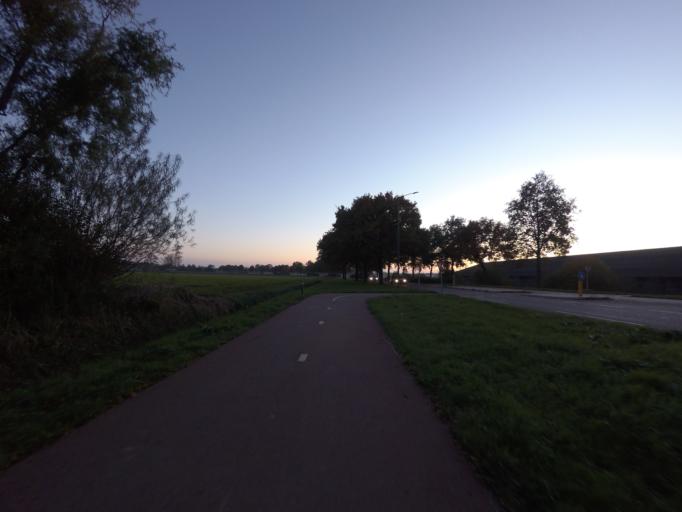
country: NL
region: North Brabant
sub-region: Gemeente Woudrichem
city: Almkerk
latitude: 51.7812
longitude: 4.9624
